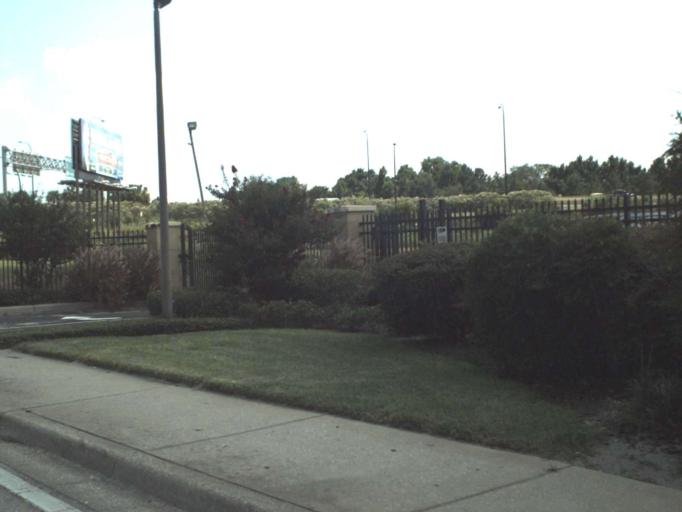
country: US
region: Florida
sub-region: Orange County
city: Orlando
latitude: 28.5444
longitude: -81.4138
